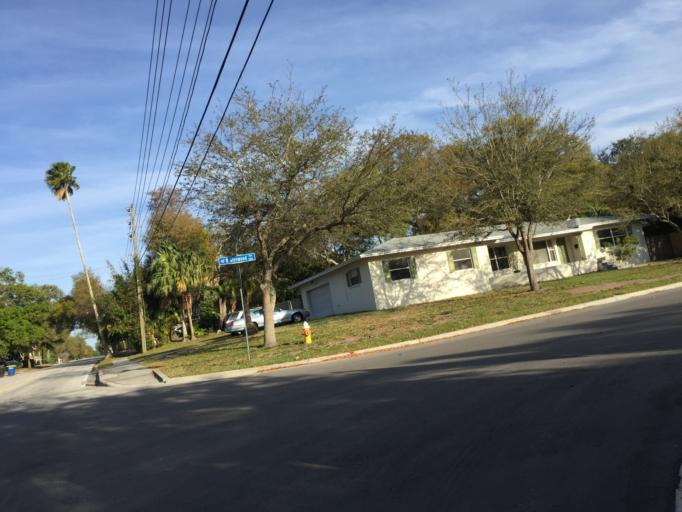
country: US
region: Florida
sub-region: Pinellas County
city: Clearwater
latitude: 27.9754
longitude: -82.7746
